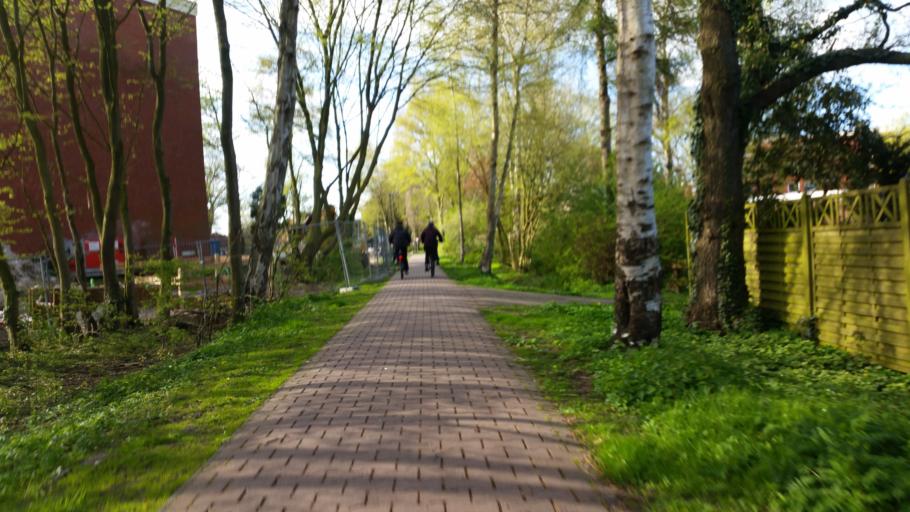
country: DE
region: Lower Saxony
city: Aurich
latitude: 53.4612
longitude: 7.4985
